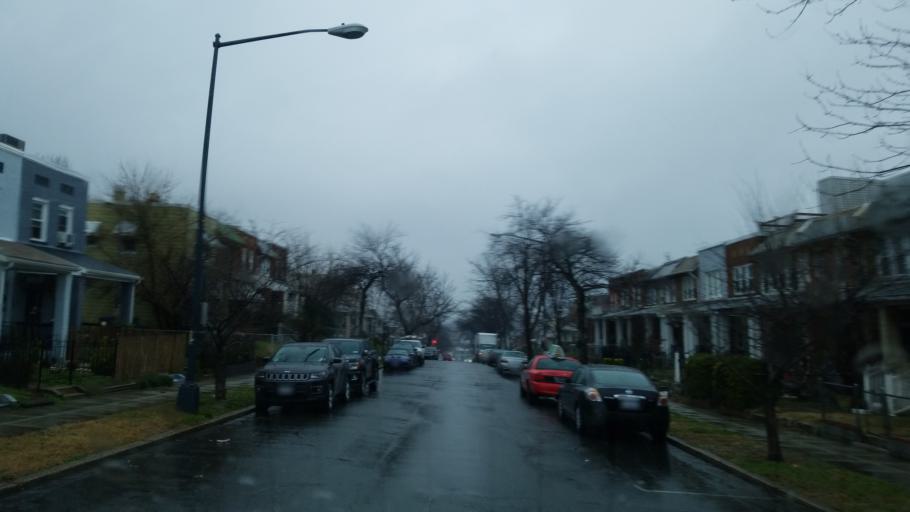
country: US
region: Maryland
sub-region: Prince George's County
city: Mount Rainier
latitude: 38.9037
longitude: -76.9773
